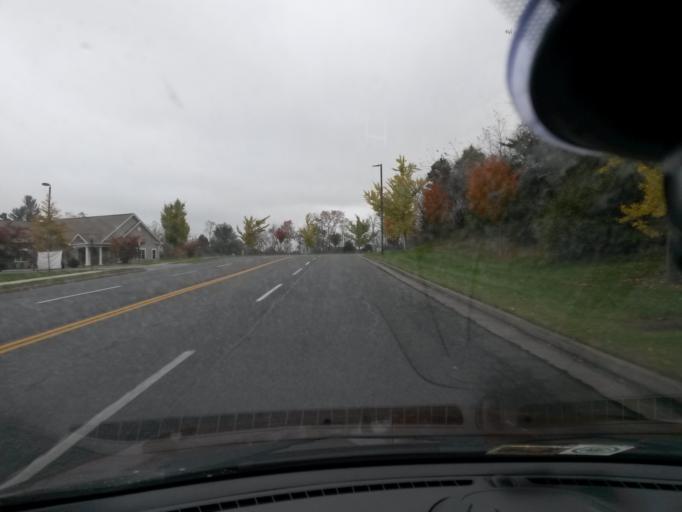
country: US
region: Virginia
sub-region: Roanoke County
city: Vinton
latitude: 37.3094
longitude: -79.8916
